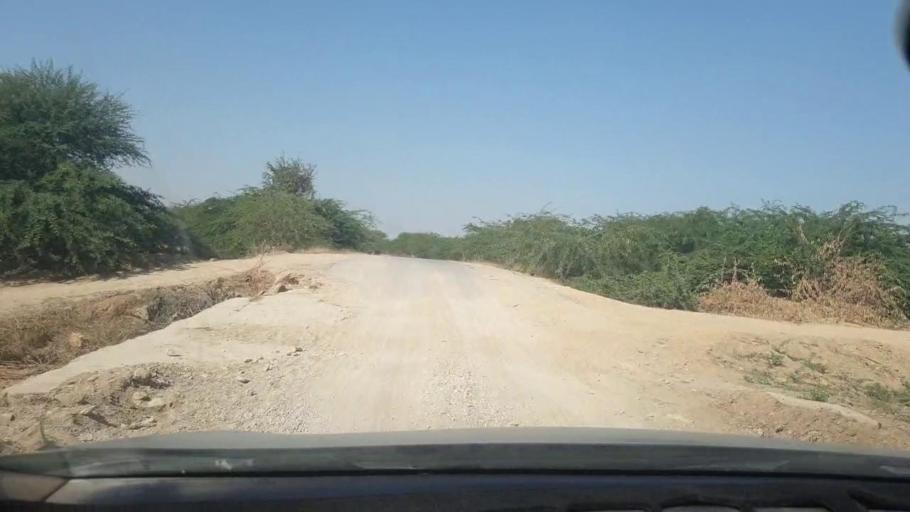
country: PK
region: Sindh
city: Malir Cantonment
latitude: 25.1614
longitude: 67.1612
